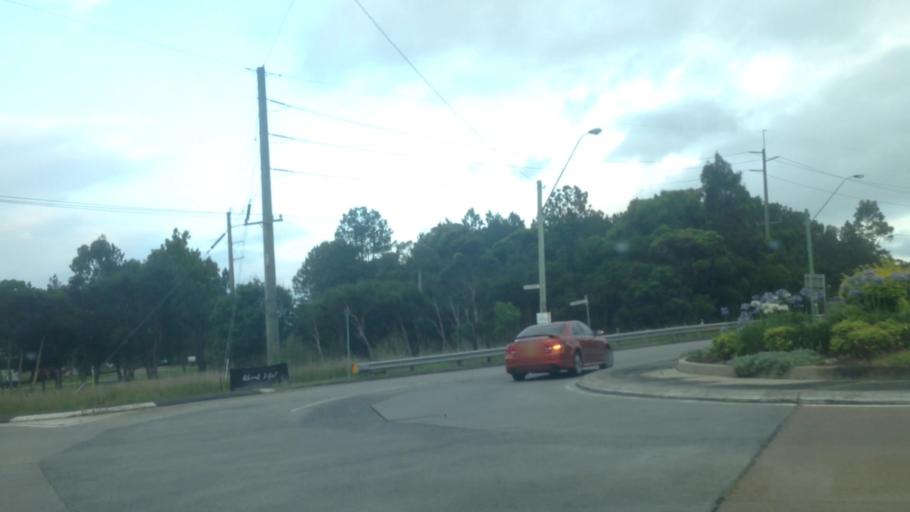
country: AU
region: New South Wales
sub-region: Lake Macquarie Shire
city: Cooranbong
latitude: -33.1161
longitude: 151.4700
